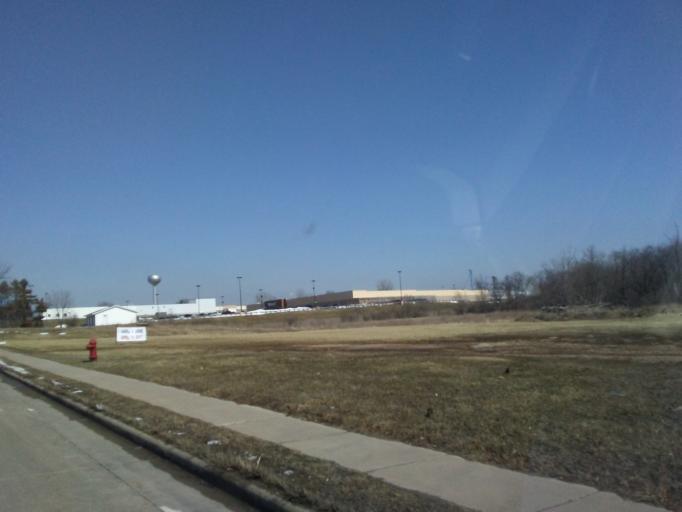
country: US
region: Wisconsin
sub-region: Vernon County
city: Viroqua
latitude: 43.5677
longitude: -90.8889
